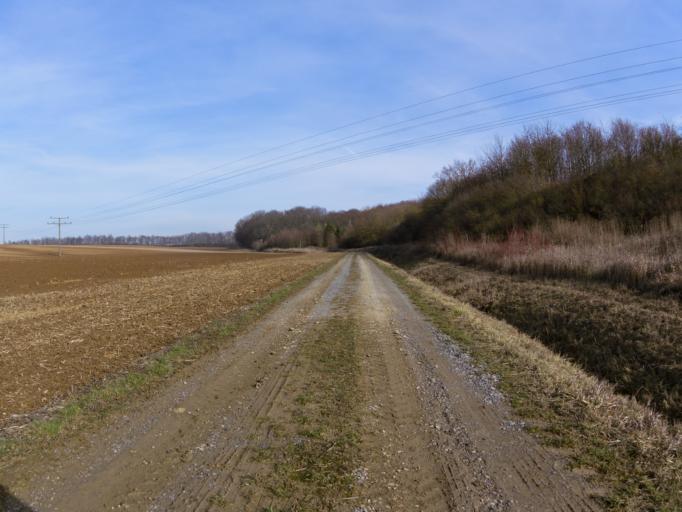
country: DE
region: Bavaria
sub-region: Regierungsbezirk Unterfranken
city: Kurnach
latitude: 49.8282
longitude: 10.0326
